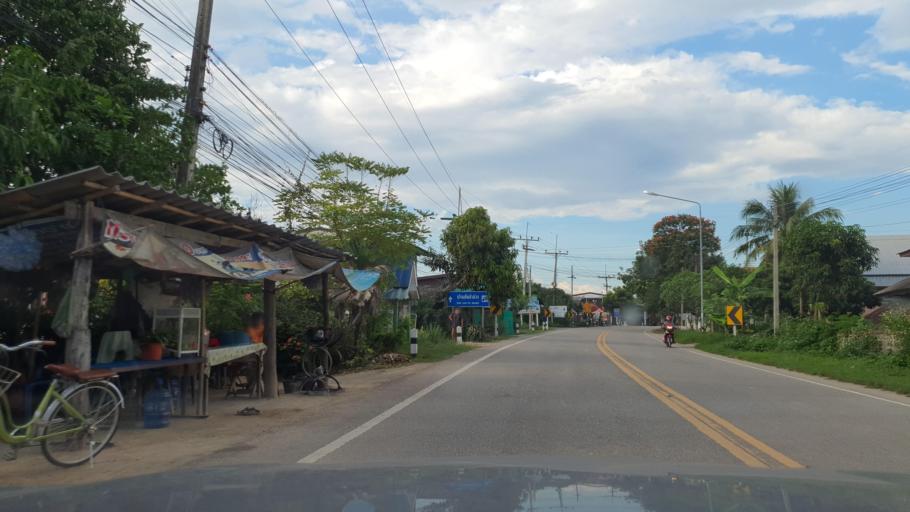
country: TH
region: Phayao
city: Phayao
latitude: 19.1730
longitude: 99.8334
